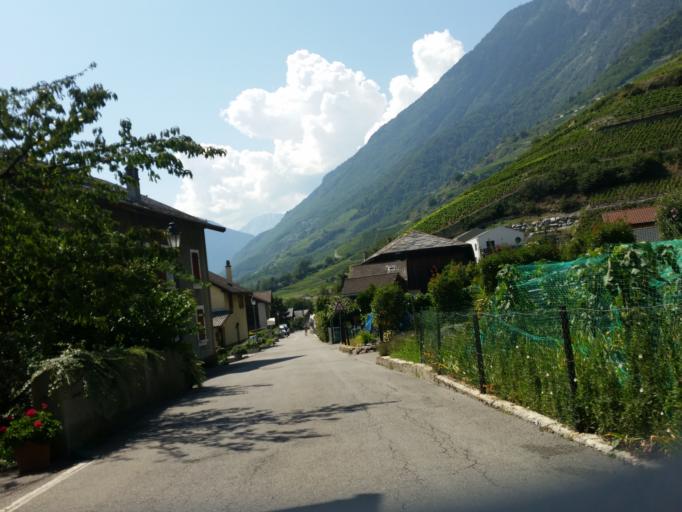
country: CH
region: Valais
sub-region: Martigny District
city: Fully
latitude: 46.1510
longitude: 7.1370
